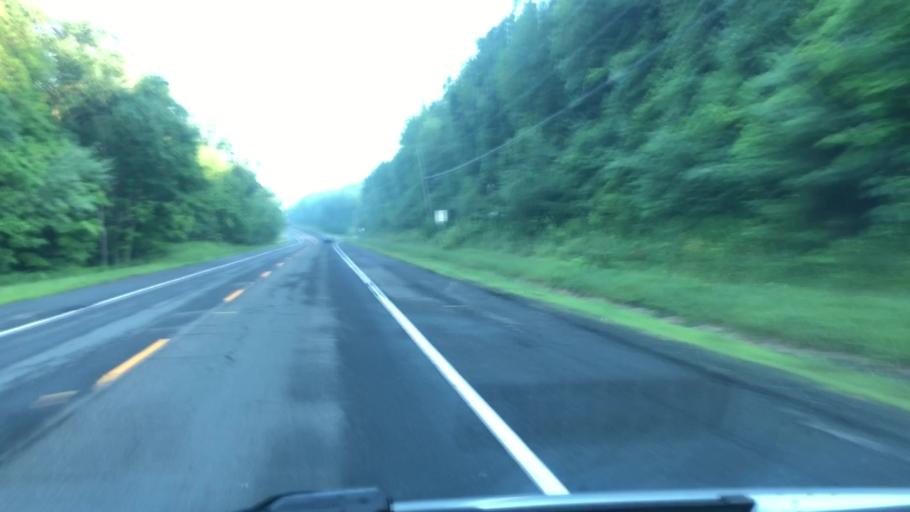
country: US
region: Massachusetts
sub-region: Berkshire County
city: Hinsdale
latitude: 42.4894
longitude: -72.9950
